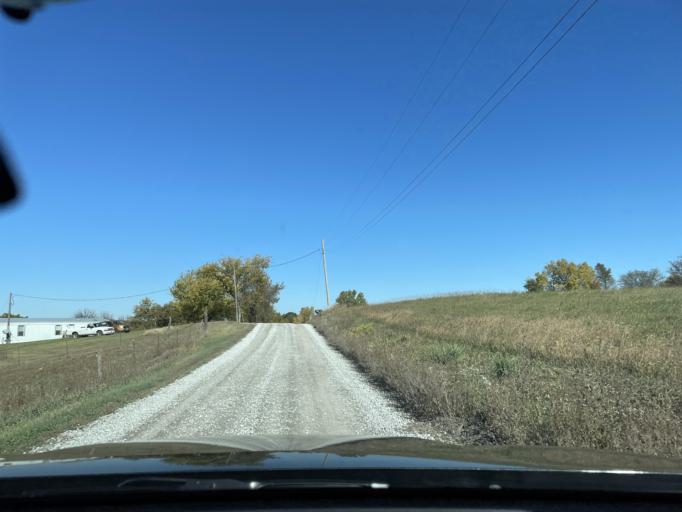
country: US
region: Missouri
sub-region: Andrew County
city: Savannah
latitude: 39.9327
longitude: -94.8805
